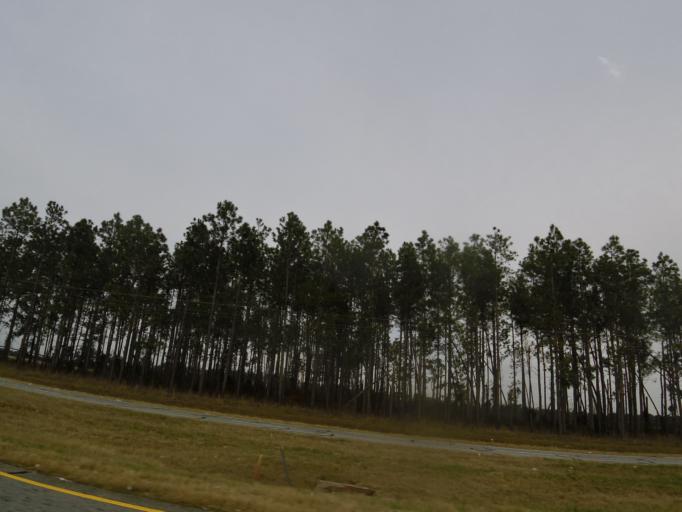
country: US
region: Georgia
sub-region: Decatur County
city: Bainbridge
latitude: 30.9629
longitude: -84.7221
